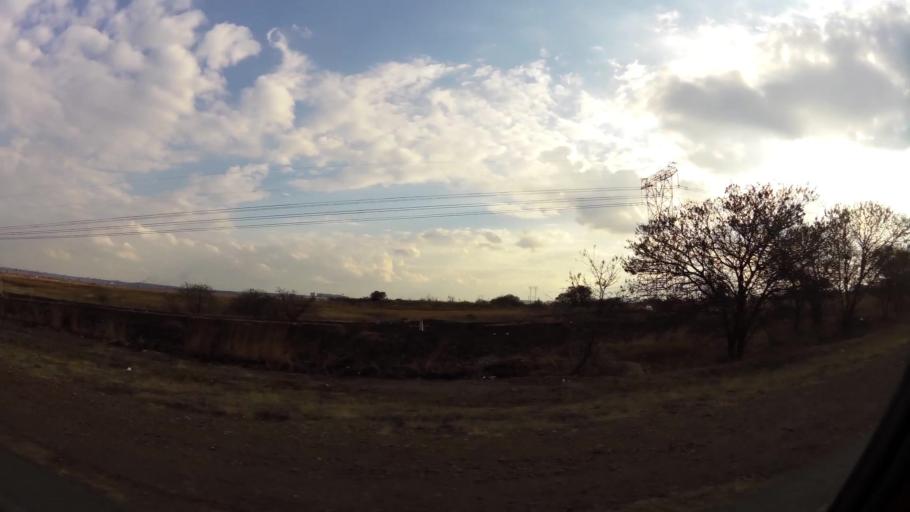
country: ZA
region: Gauteng
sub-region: Sedibeng District Municipality
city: Vereeniging
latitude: -26.6463
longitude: 27.8756
